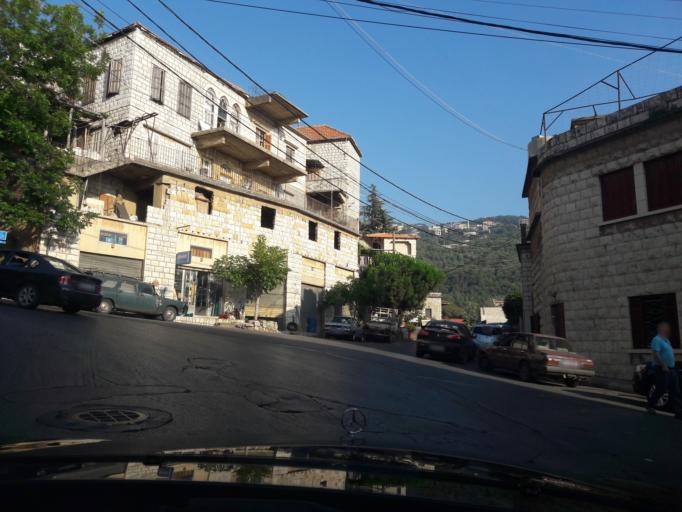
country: LB
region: Mont-Liban
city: Djounie
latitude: 33.9276
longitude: 35.6715
